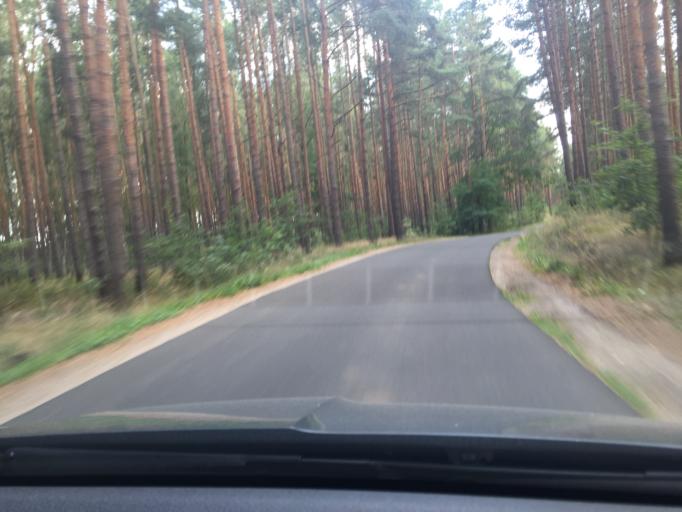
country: DE
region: Brandenburg
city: Grunheide
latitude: 52.3696
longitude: 13.7888
